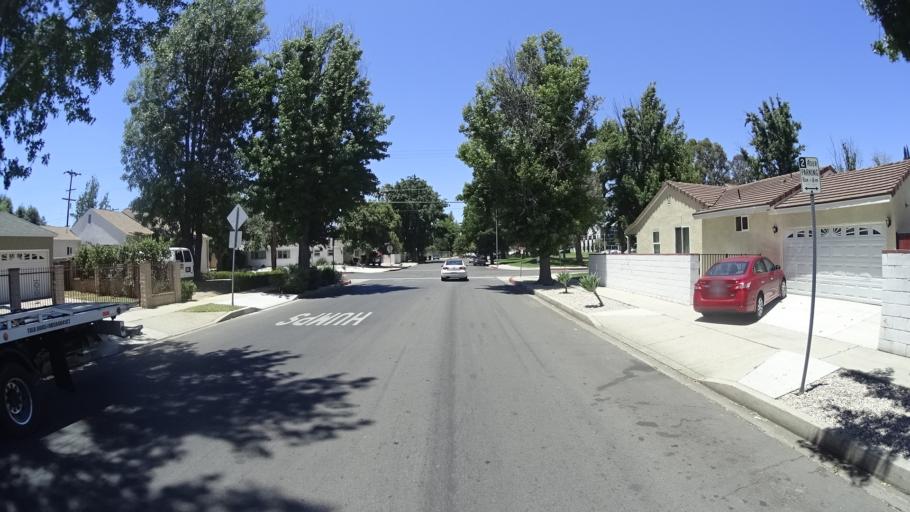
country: US
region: California
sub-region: Los Angeles County
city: Van Nuys
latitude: 34.2121
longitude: -118.4702
